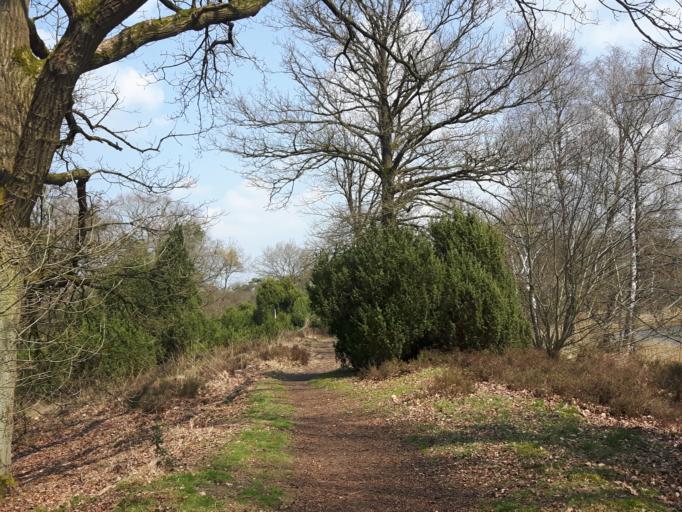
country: NL
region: Overijssel
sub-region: Gemeente Haaksbergen
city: Haaksbergen
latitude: 52.1651
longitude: 6.8085
